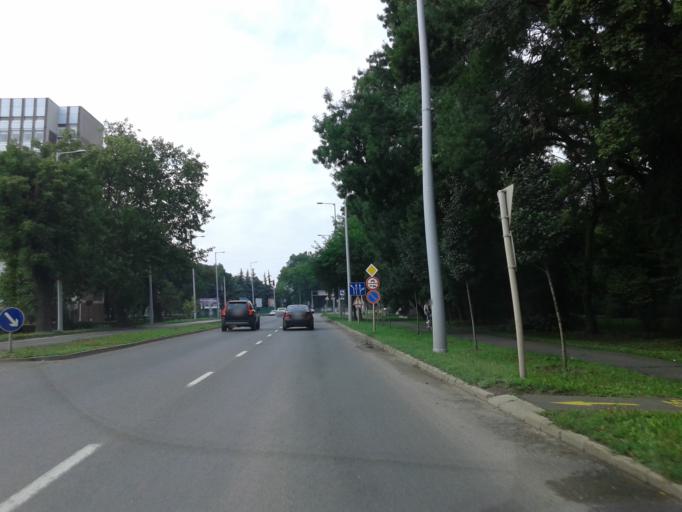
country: HU
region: Csongrad
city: Szeged
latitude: 46.2462
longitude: 20.1646
